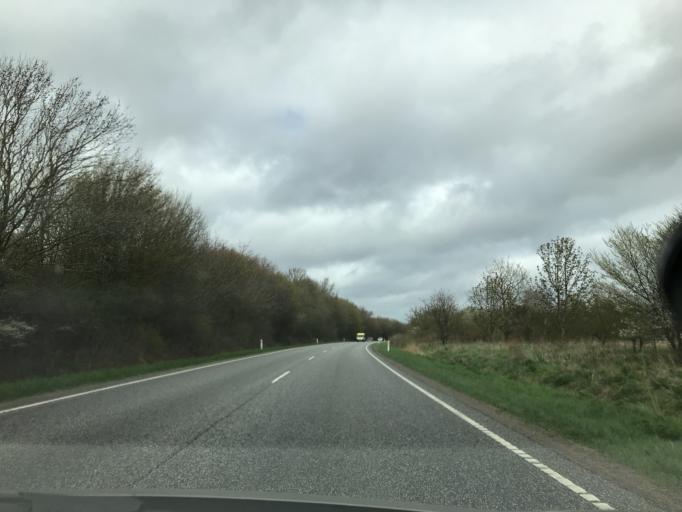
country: DK
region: Central Jutland
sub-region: Skive Kommune
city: Skive
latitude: 56.5726
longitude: 9.0051
